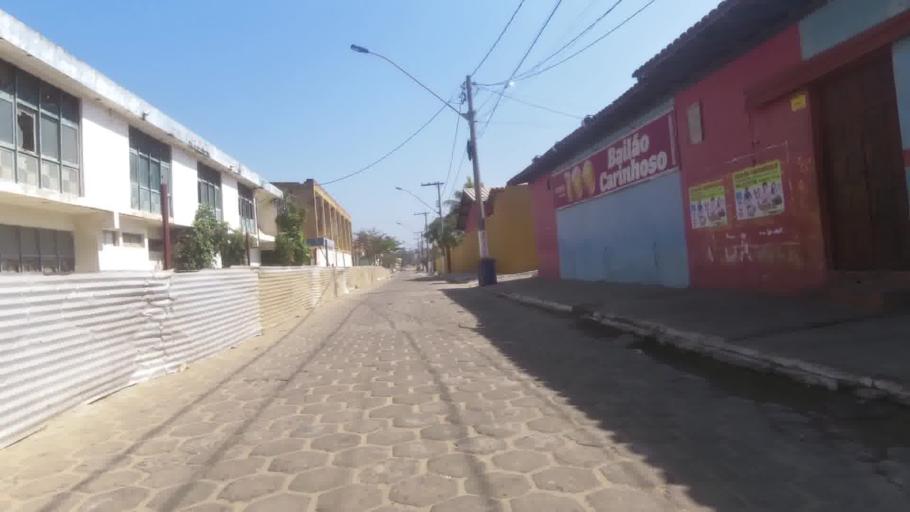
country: BR
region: Espirito Santo
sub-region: Marataizes
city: Marataizes
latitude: -21.0423
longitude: -40.8226
